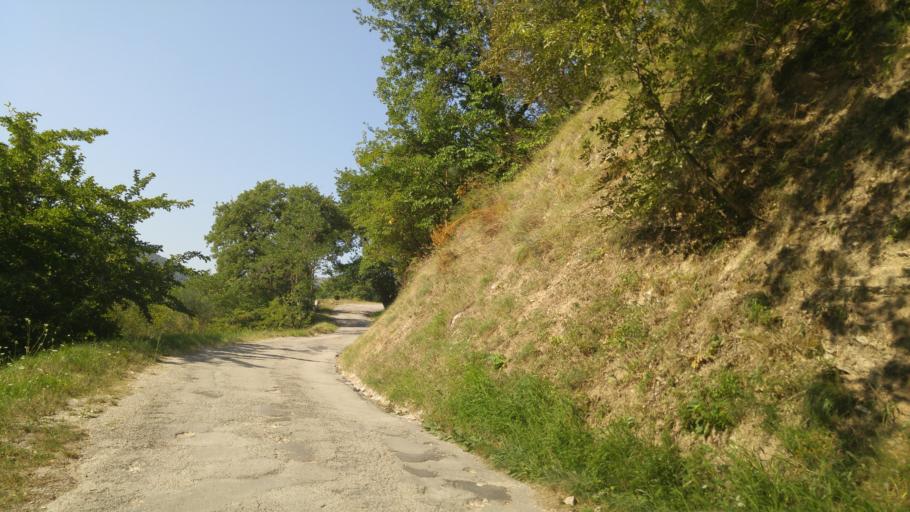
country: IT
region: The Marches
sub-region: Provincia di Pesaro e Urbino
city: Fossombrone
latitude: 43.6796
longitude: 12.8031
